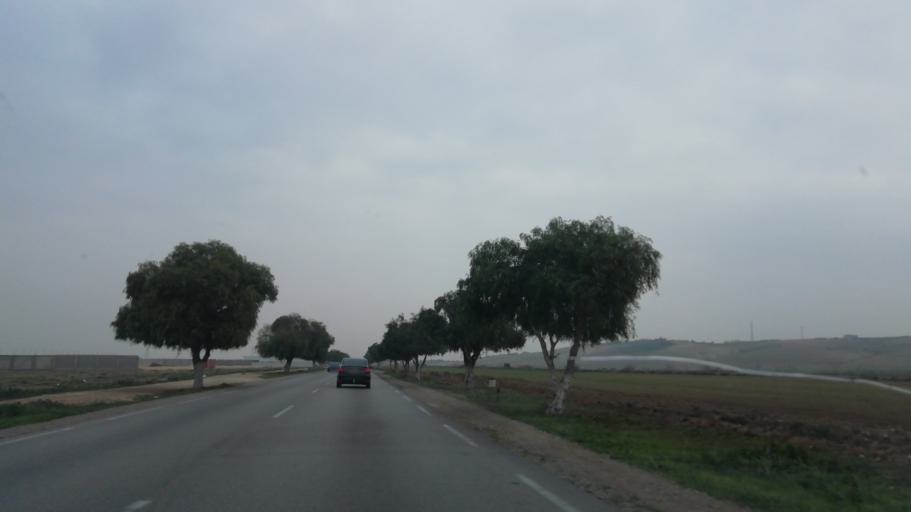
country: DZ
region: Mascara
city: Sig
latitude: 35.5512
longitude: -0.2746
